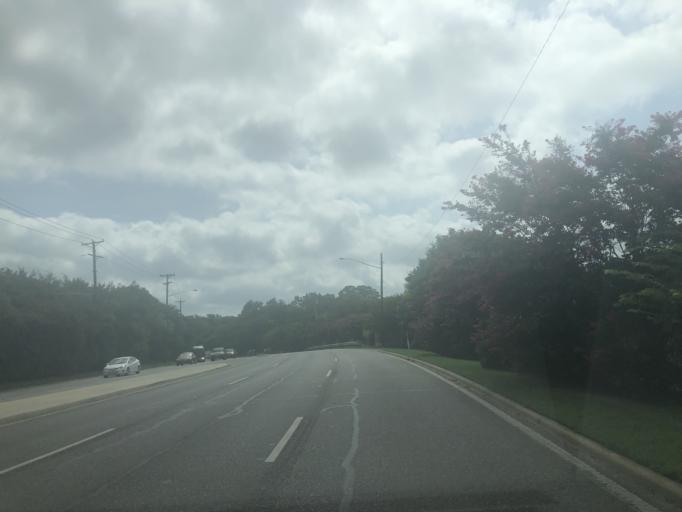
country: US
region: Texas
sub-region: Dallas County
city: University Park
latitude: 32.8633
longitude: -96.8323
